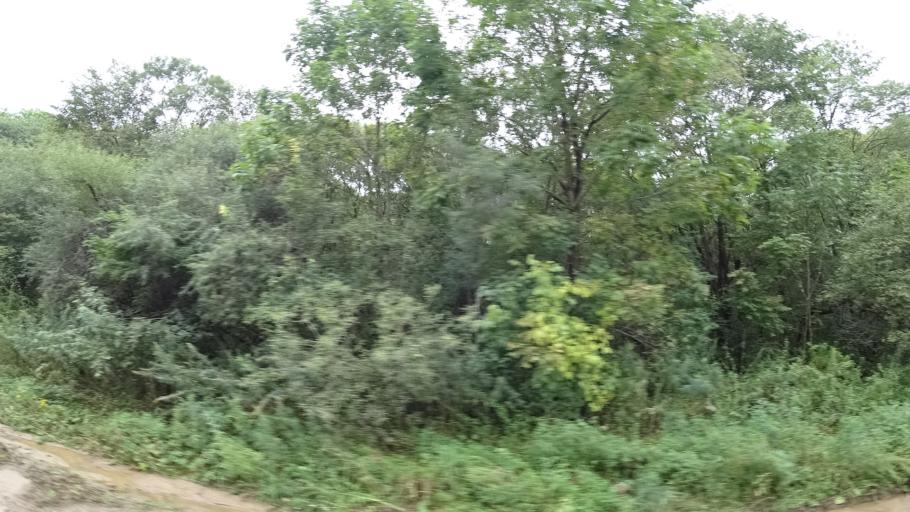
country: RU
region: Primorskiy
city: Rettikhovka
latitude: 44.0601
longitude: 132.6543
